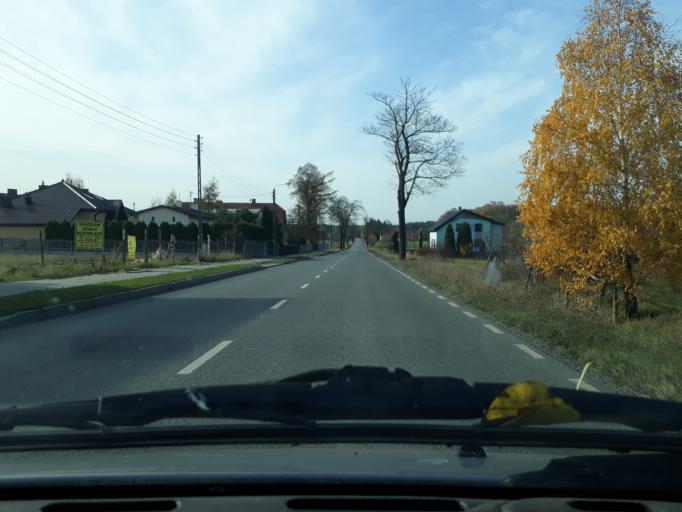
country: PL
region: Silesian Voivodeship
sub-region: Powiat lubliniecki
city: Psary
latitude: 50.5767
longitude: 18.9869
